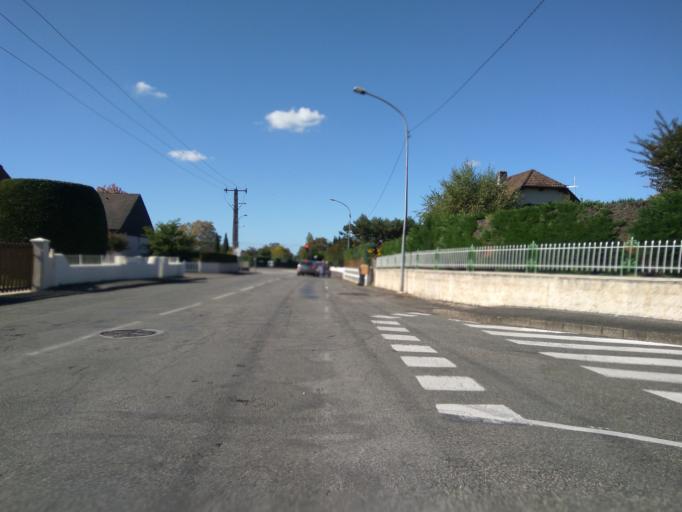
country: FR
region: Aquitaine
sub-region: Departement des Pyrenees-Atlantiques
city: Idron
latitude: 43.3023
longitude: -0.3288
